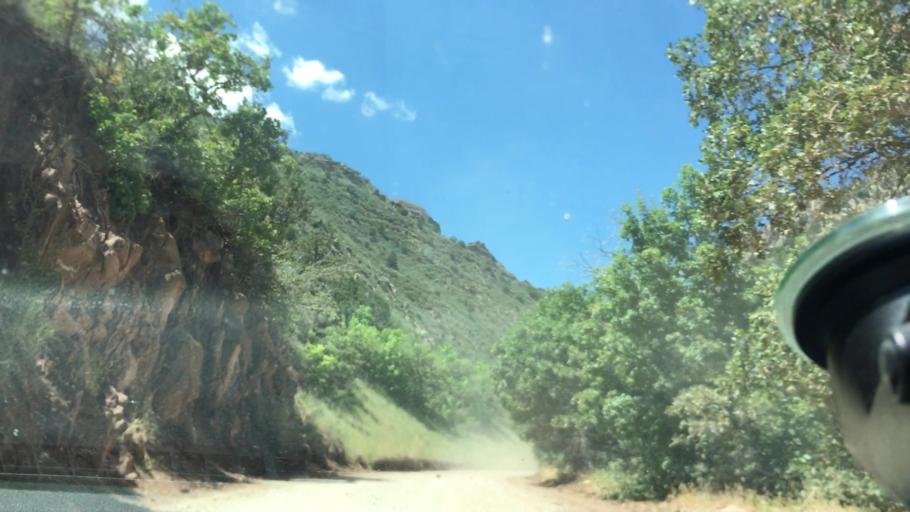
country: US
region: Utah
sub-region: Sanpete County
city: Moroni
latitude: 39.5553
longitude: -111.6616
